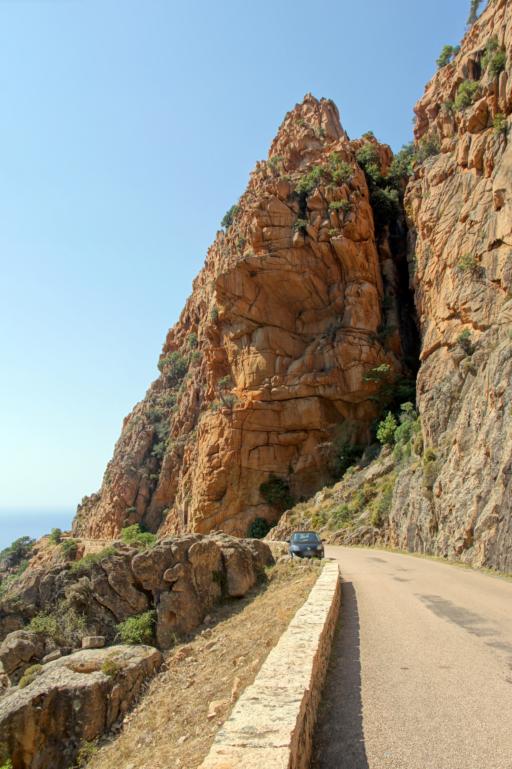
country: FR
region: Corsica
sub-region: Departement de la Corse-du-Sud
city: Cargese
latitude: 42.2481
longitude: 8.6596
